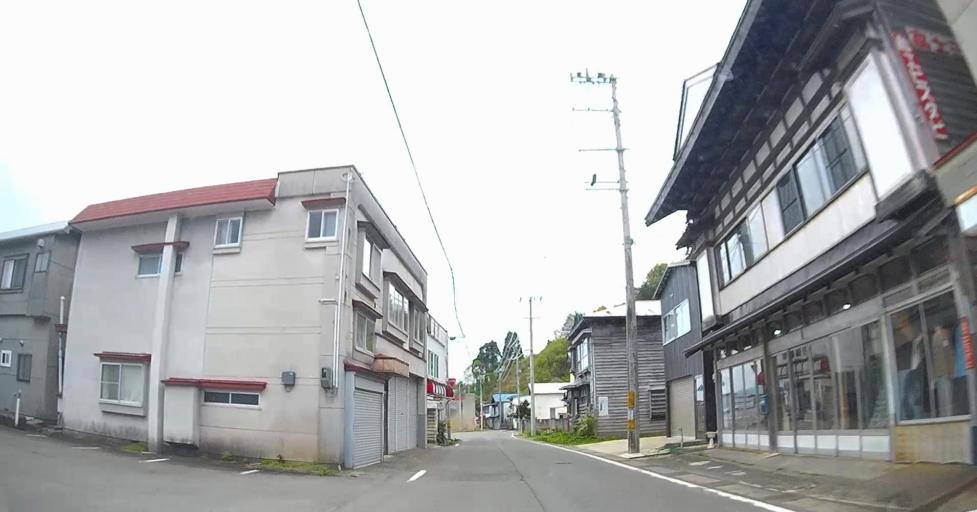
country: JP
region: Aomori
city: Shimokizukuri
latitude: 41.1964
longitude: 140.4303
